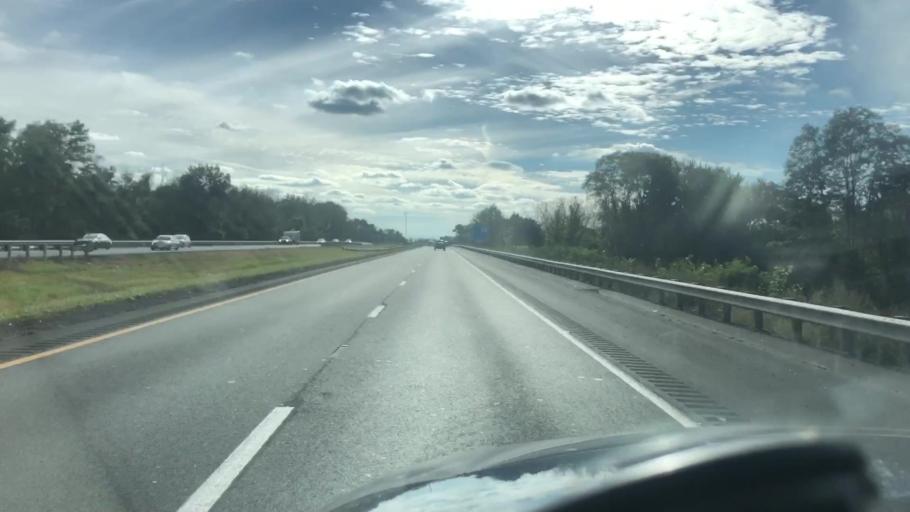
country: US
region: Massachusetts
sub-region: Hampshire County
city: Northampton
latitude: 42.3112
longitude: -72.6204
